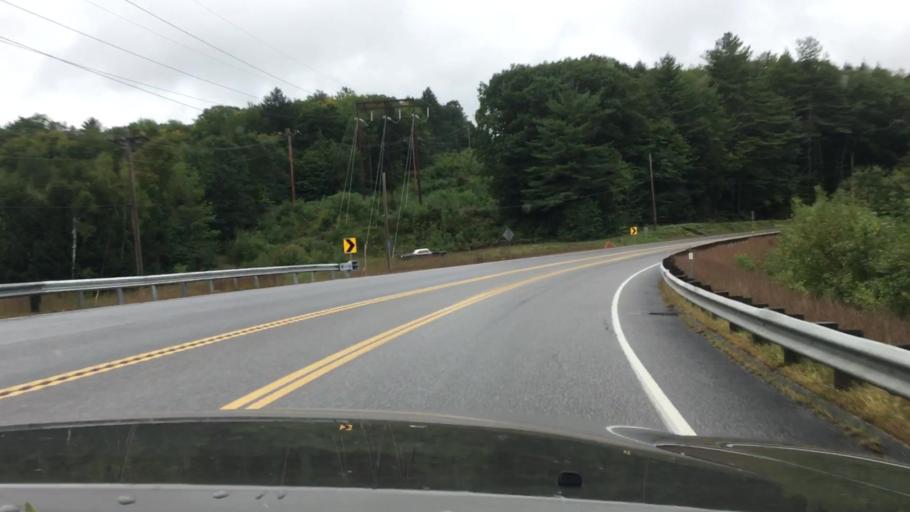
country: US
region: New Hampshire
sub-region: Hillsborough County
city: Antrim
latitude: 43.0750
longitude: -71.9826
